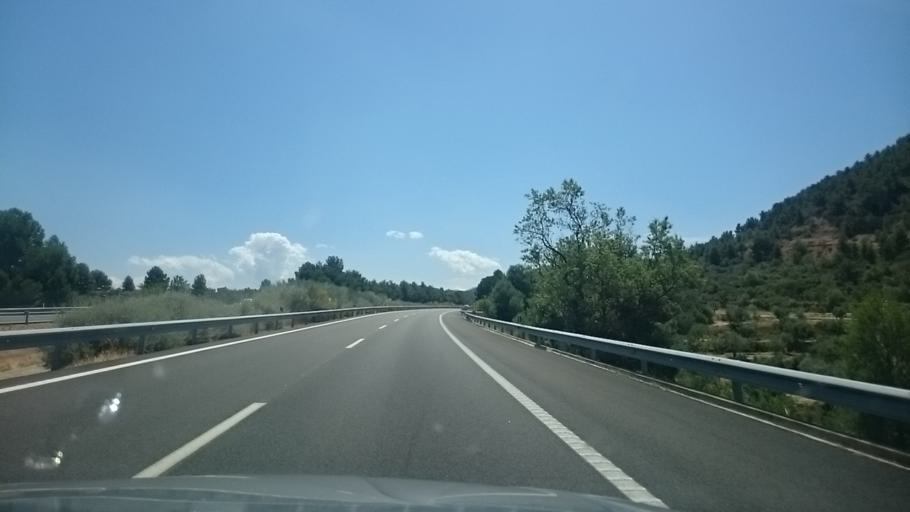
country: ES
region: Catalonia
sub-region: Provincia de Lleida
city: Vinaixa
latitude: 41.4530
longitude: 0.8976
